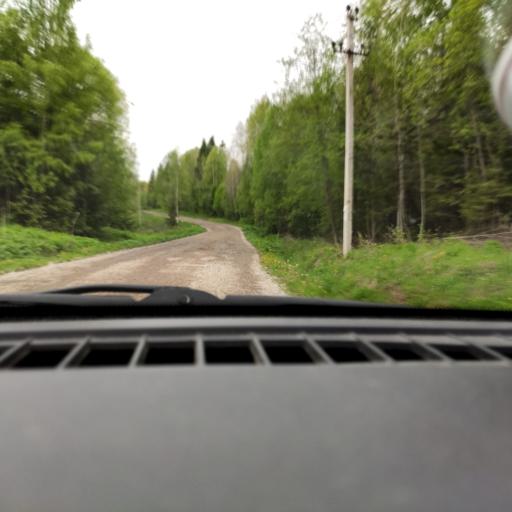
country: RU
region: Perm
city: Polazna
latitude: 58.2915
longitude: 56.1583
